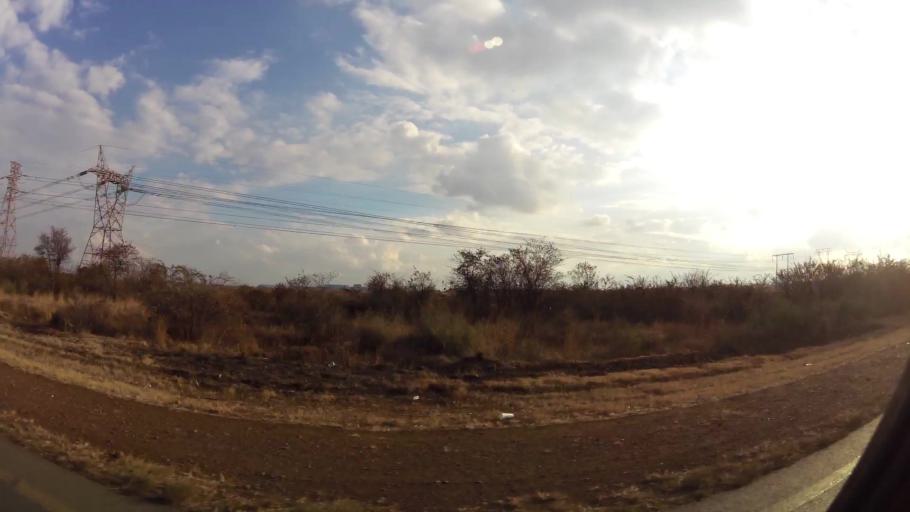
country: ZA
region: Gauteng
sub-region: Sedibeng District Municipality
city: Vereeniging
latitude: -26.6268
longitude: 27.8657
